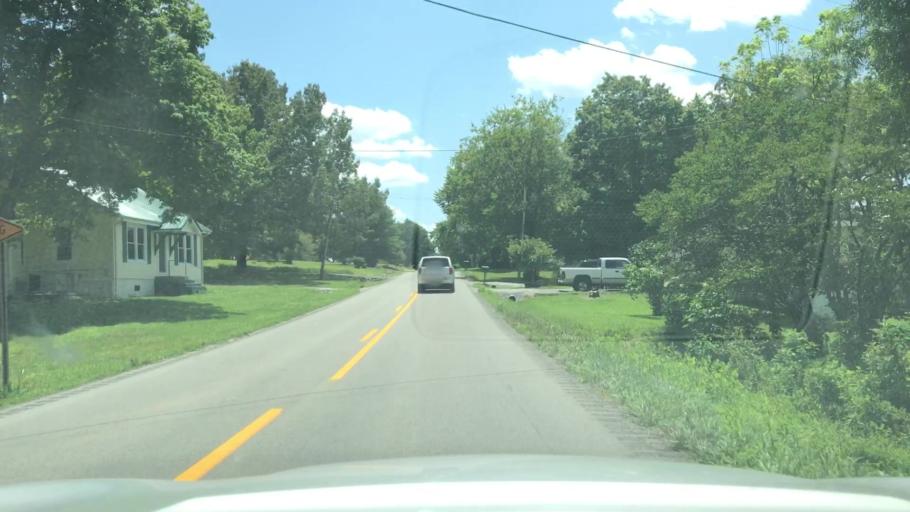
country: US
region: Kentucky
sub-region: Christian County
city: Hopkinsville
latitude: 36.9028
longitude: -87.4477
